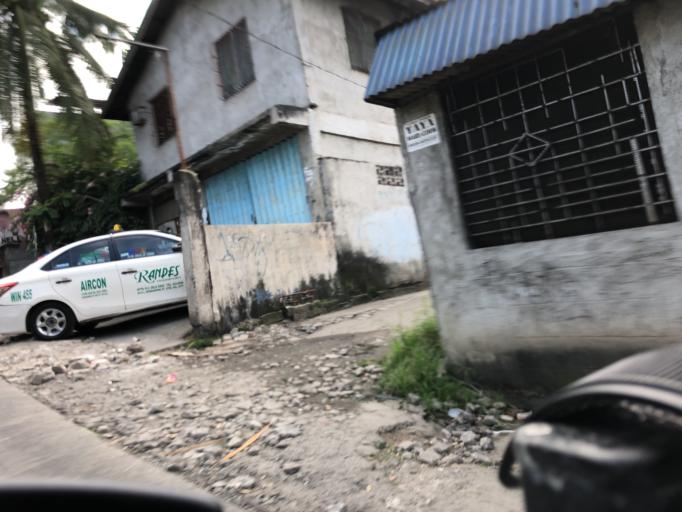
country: PH
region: Central Luzon
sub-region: Province of Bulacan
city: San Jose del Monte
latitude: 14.7427
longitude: 121.0606
